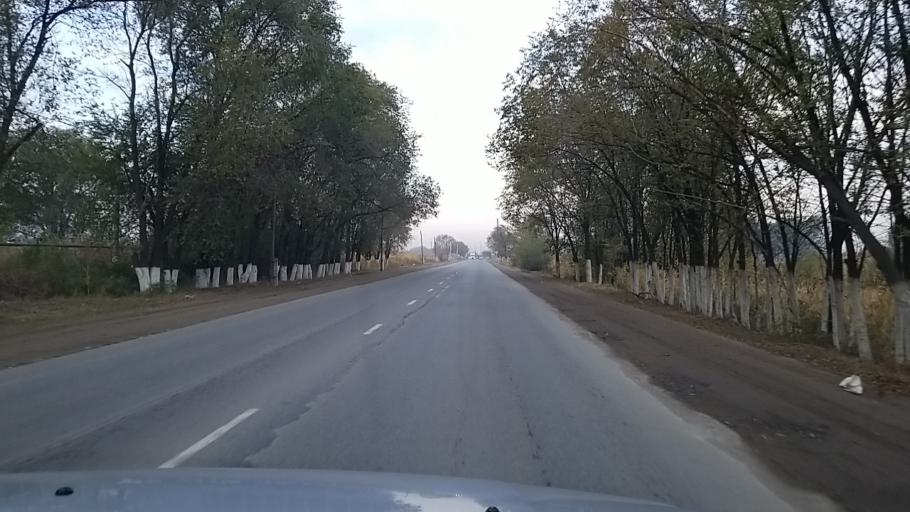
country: KZ
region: Almaty Oblysy
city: Burunday
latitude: 43.3566
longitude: 76.7921
